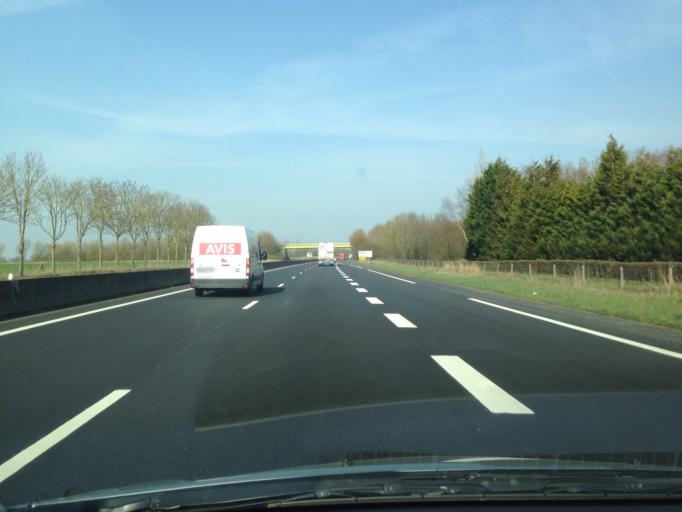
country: FR
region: Picardie
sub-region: Departement de la Somme
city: Abbeville
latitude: 50.0454
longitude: 1.7624
